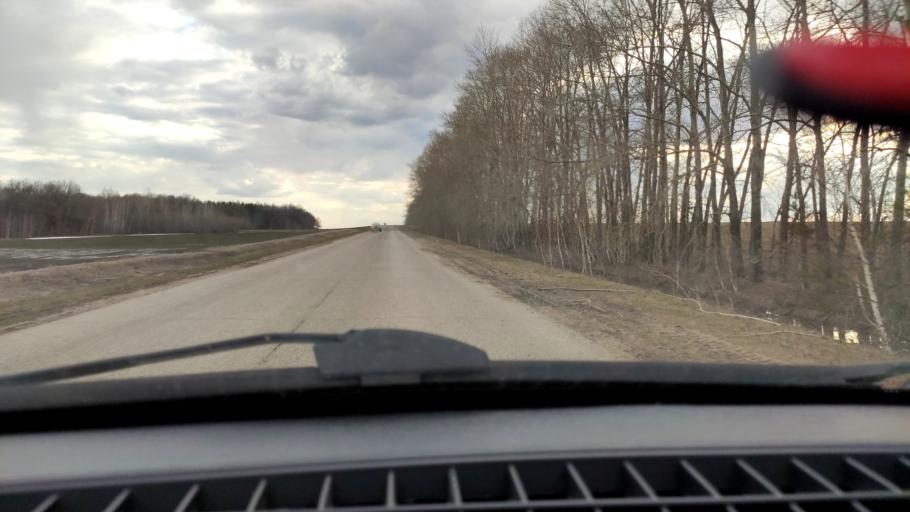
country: RU
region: Bashkortostan
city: Karmaskaly
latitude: 54.3035
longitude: 55.9315
